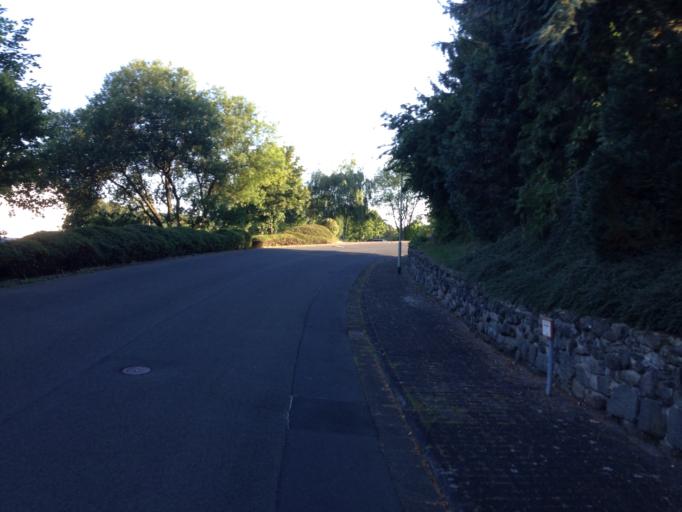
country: DE
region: Hesse
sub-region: Regierungsbezirk Giessen
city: Lich
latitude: 50.5446
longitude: 8.7788
